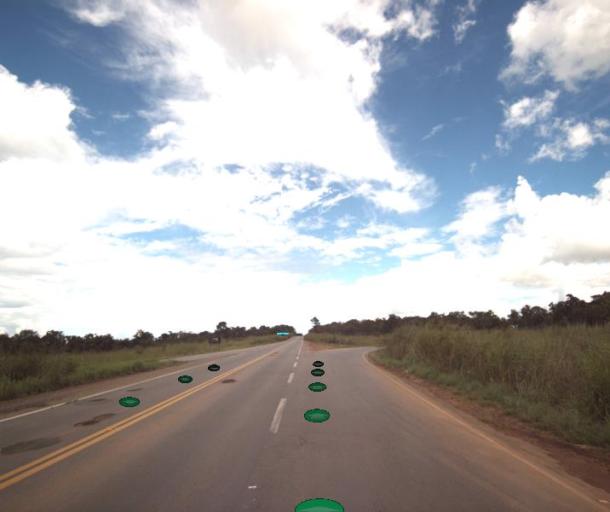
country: BR
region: Goias
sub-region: Jaragua
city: Jaragua
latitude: -15.8914
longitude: -49.2387
